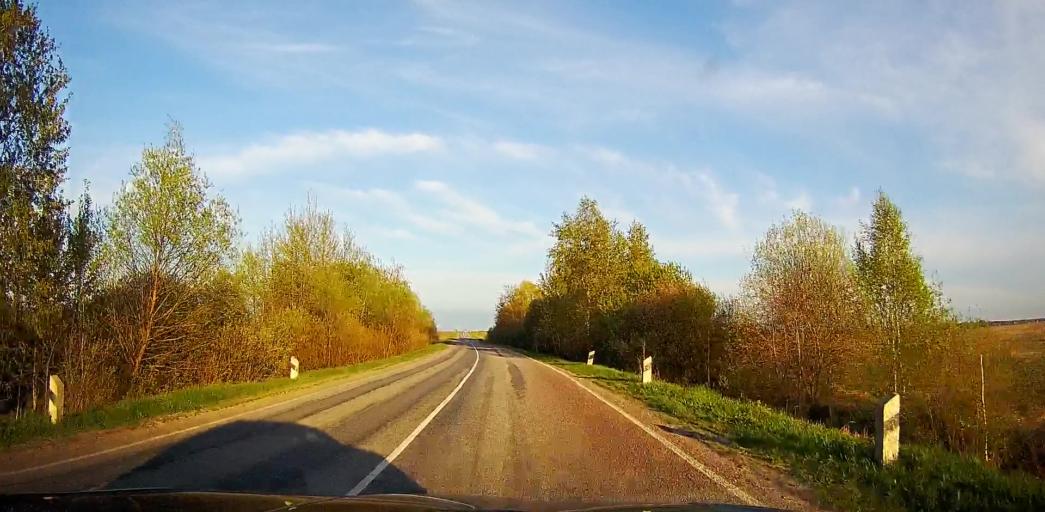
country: RU
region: Moskovskaya
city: Bronnitsy
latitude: 55.2754
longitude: 38.2261
